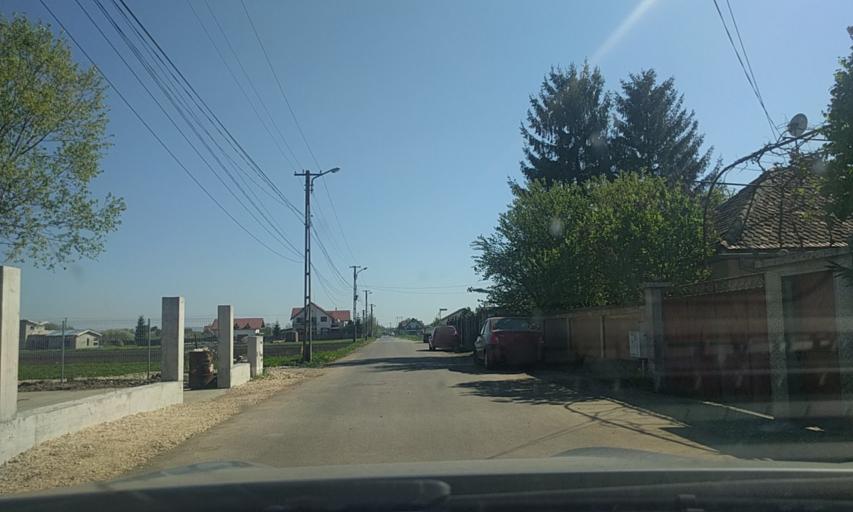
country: RO
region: Brasov
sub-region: Comuna Ghimbav
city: Ghimbav
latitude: 45.7011
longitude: 25.5478
